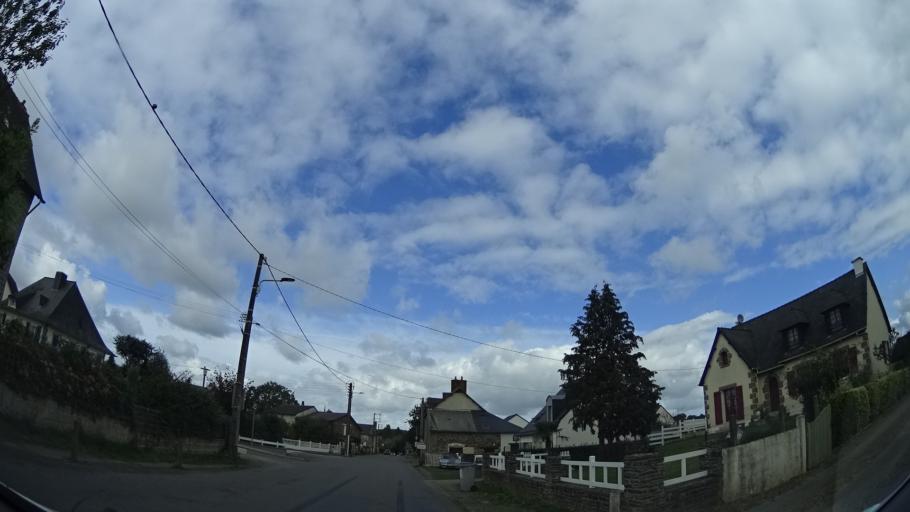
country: FR
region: Brittany
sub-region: Departement d'Ille-et-Vilaine
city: Montreuil-sur-Ille
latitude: 48.3050
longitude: -1.6656
